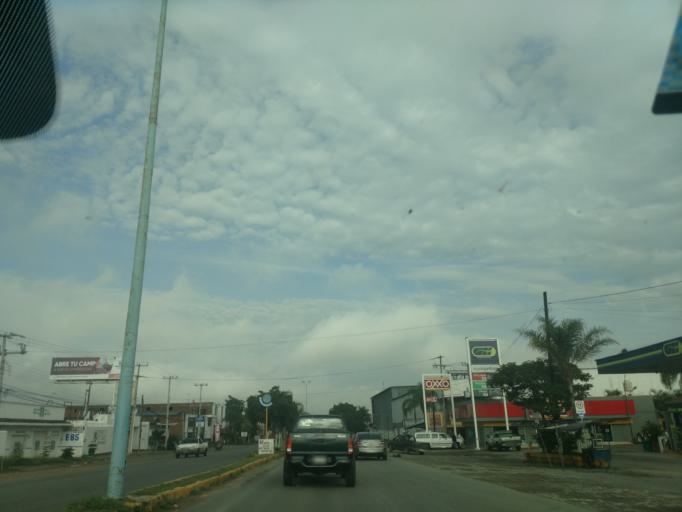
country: MX
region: Jalisco
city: Ameca
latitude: 20.5356
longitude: -104.0283
